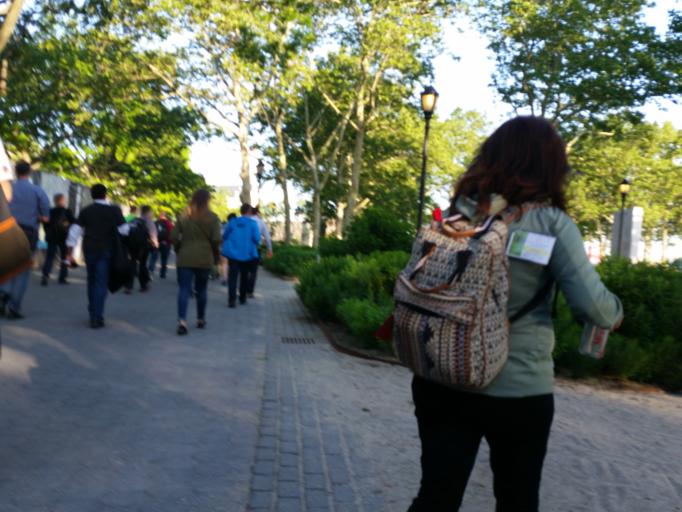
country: US
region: New York
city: New York City
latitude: 40.7027
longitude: -74.0161
